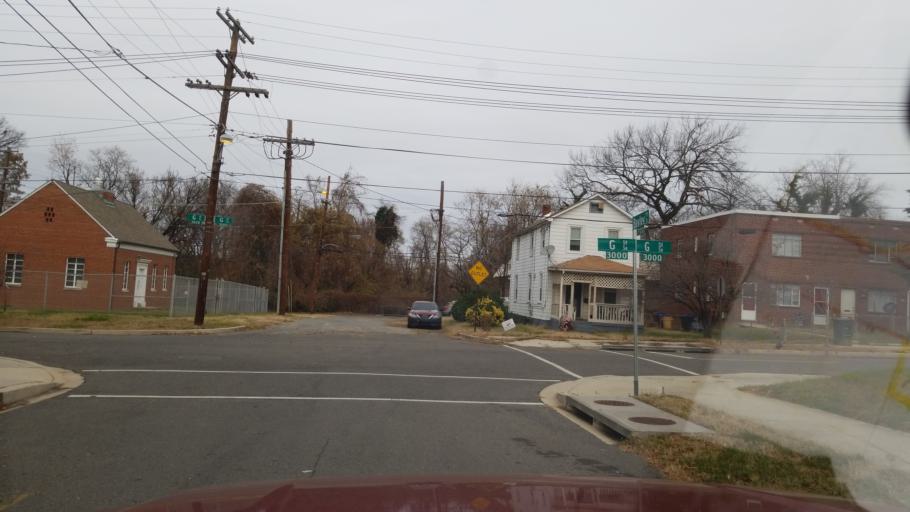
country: US
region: Maryland
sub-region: Prince George's County
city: Silver Hill
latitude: 38.8801
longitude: -76.9639
